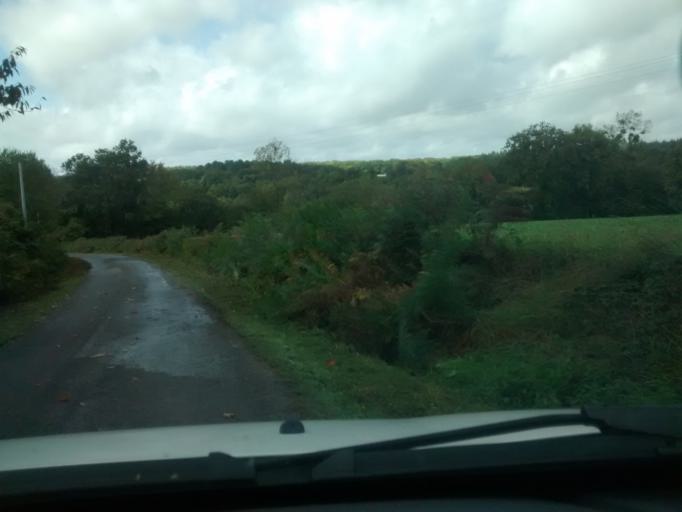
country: FR
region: Brittany
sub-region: Departement d'Ille-et-Vilaine
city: Chateaubourg
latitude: 48.1344
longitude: -1.4197
